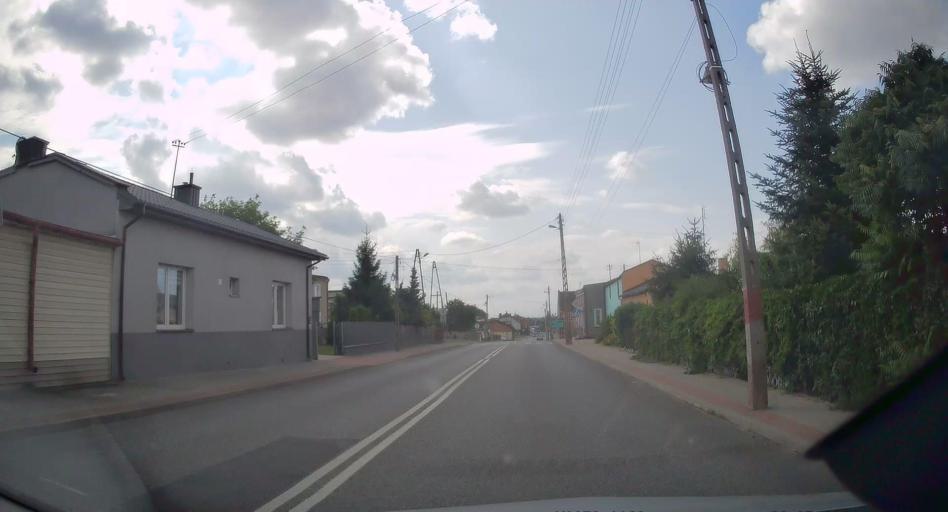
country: PL
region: Lodz Voivodeship
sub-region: Powiat brzezinski
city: Jezow
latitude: 51.8130
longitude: 19.9719
